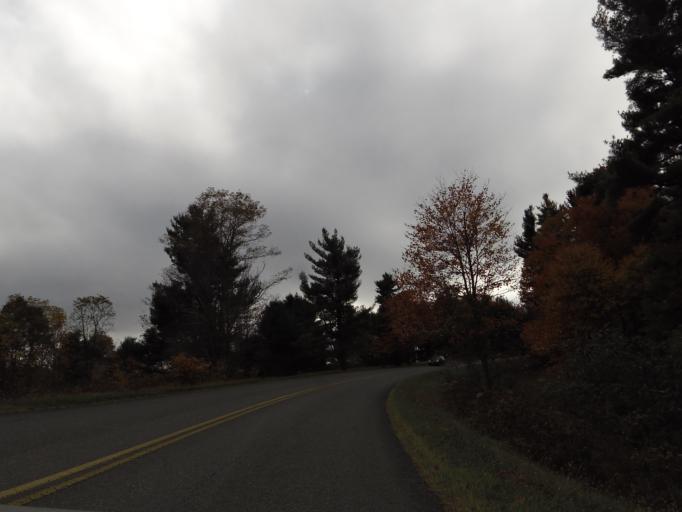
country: US
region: Virginia
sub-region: Carroll County
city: Cana
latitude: 36.6504
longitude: -80.7110
